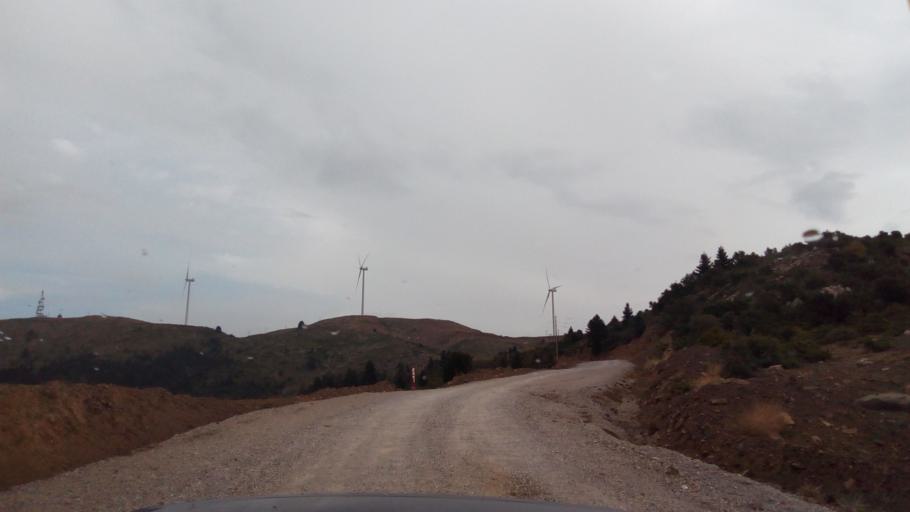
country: GR
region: Central Greece
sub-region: Nomos Fokidos
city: Lidoriki
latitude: 38.4471
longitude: 22.0728
